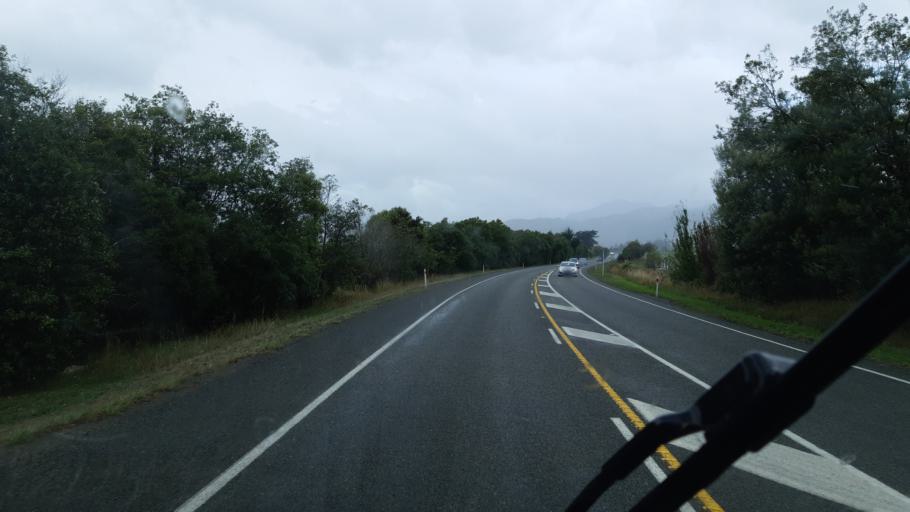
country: NZ
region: Tasman
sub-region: Tasman District
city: Brightwater
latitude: -41.3776
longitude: 173.1021
